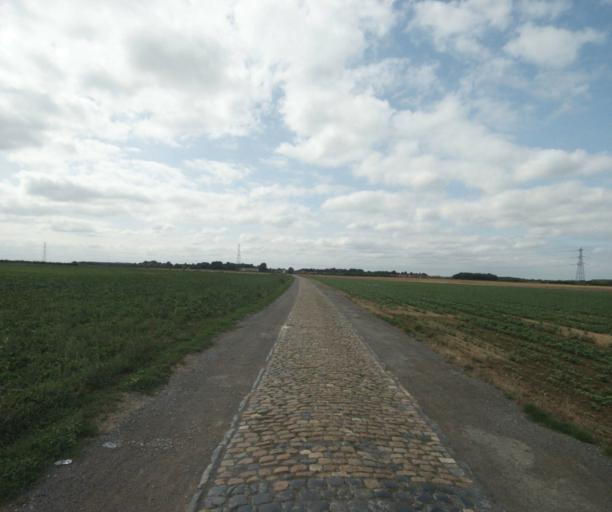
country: FR
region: Nord-Pas-de-Calais
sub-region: Departement du Nord
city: Gruson
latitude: 50.5916
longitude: 3.2264
